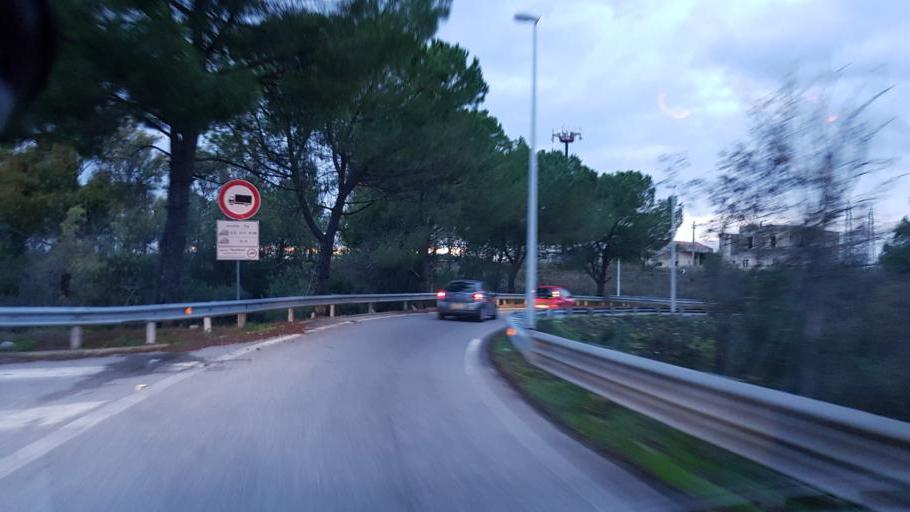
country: IT
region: Apulia
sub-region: Provincia di Taranto
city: Paolo VI
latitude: 40.5052
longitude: 17.2631
